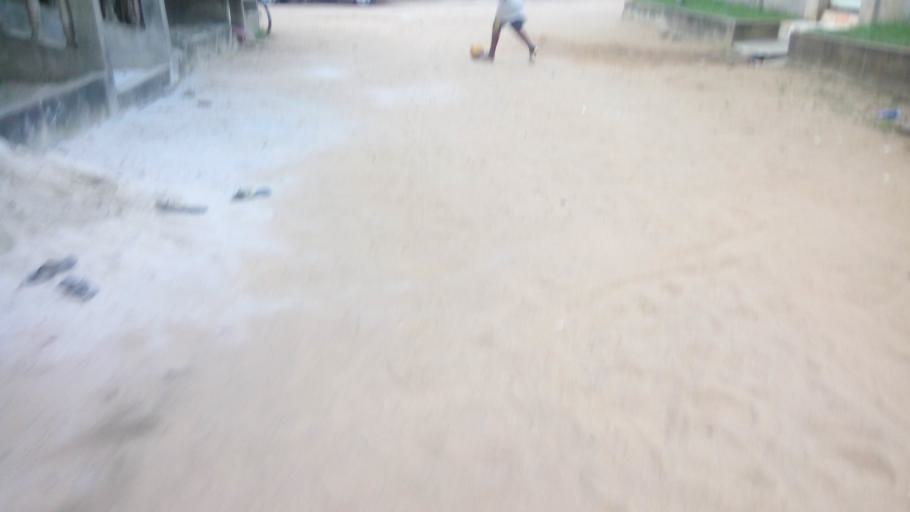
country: CI
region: Lagunes
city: Abobo
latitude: 5.4078
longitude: -3.9898
